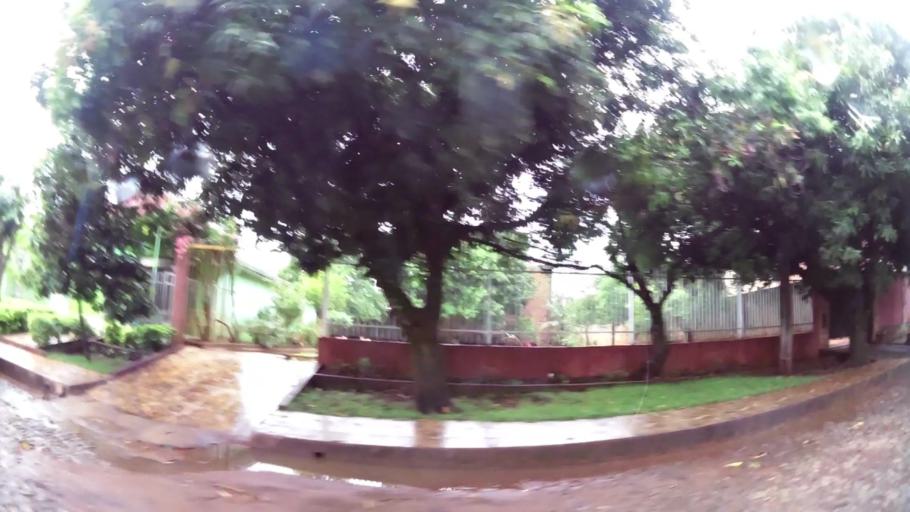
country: PY
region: Alto Parana
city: Presidente Franco
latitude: -25.5150
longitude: -54.6723
